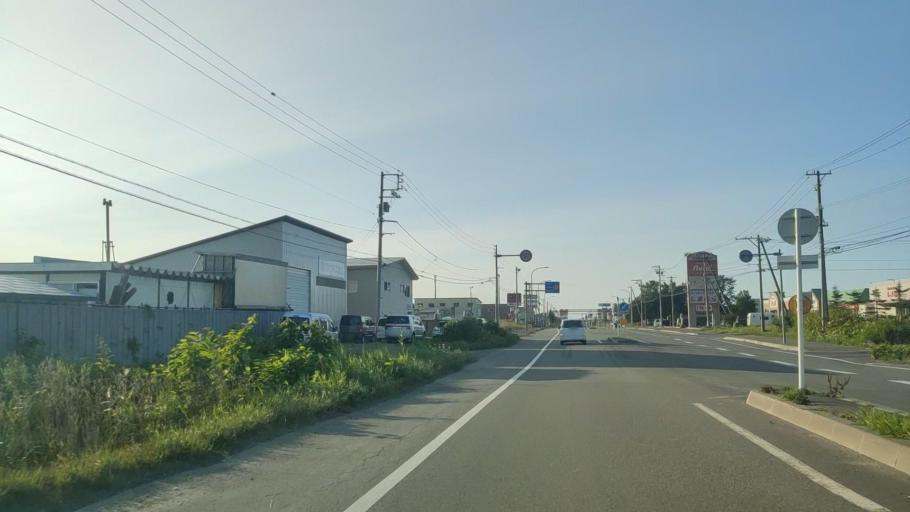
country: JP
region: Hokkaido
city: Wakkanai
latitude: 45.3788
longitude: 141.7105
